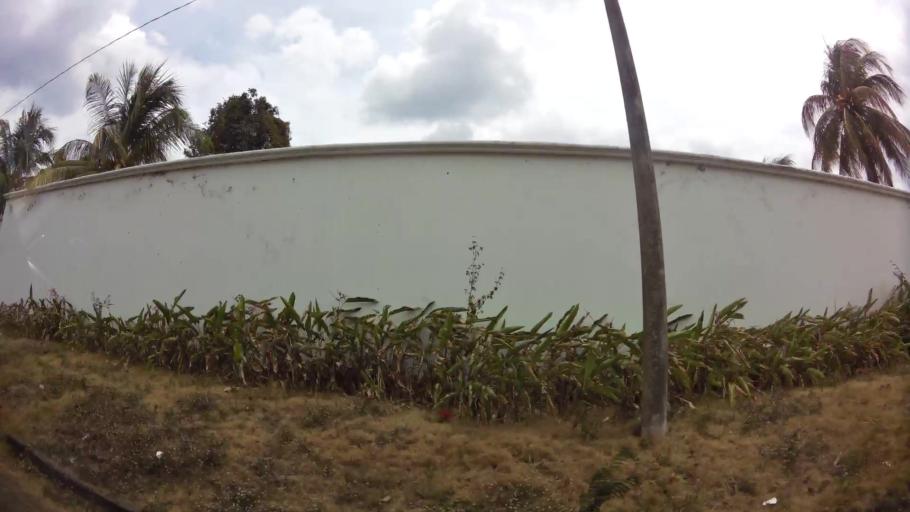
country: NI
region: Managua
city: Managua
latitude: 12.0950
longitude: -86.2262
